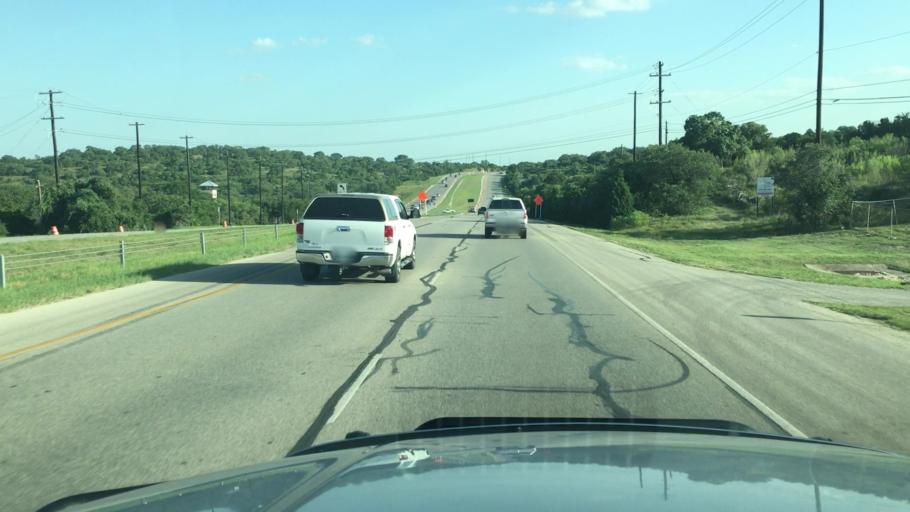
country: US
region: Texas
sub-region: Comal County
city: Bulverde
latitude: 29.7735
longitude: -98.4274
